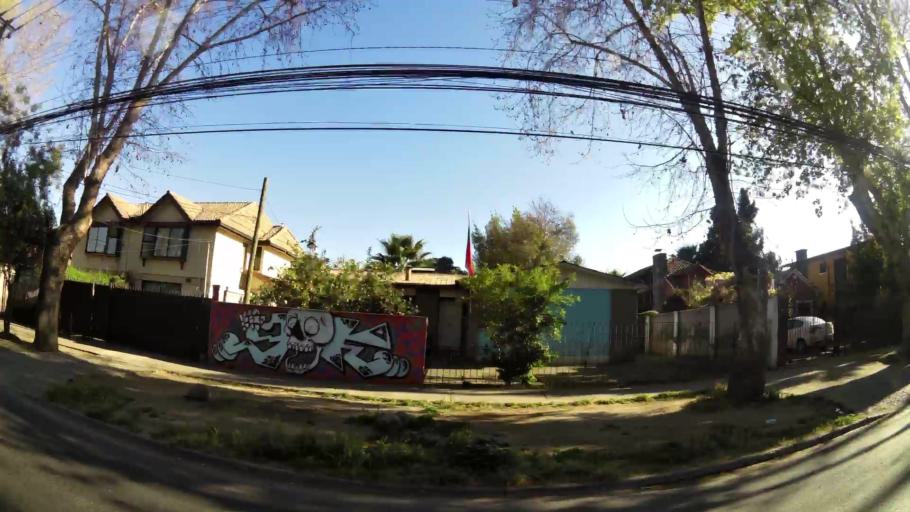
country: CL
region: Santiago Metropolitan
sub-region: Provincia de Santiago
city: Villa Presidente Frei, Nunoa, Santiago, Chile
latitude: -33.4475
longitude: -70.5674
